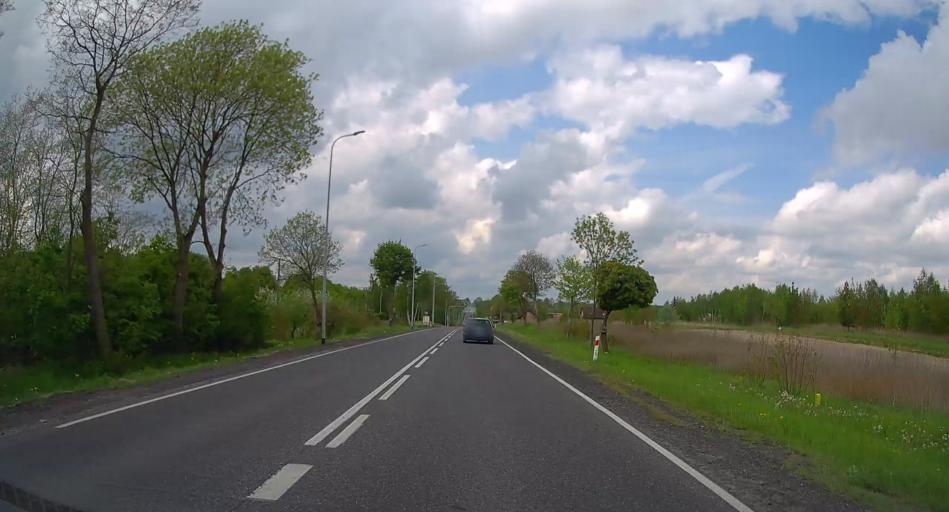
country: PL
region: Masovian Voivodeship
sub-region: Powiat nowodworski
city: Zakroczym
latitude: 52.4415
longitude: 20.5484
